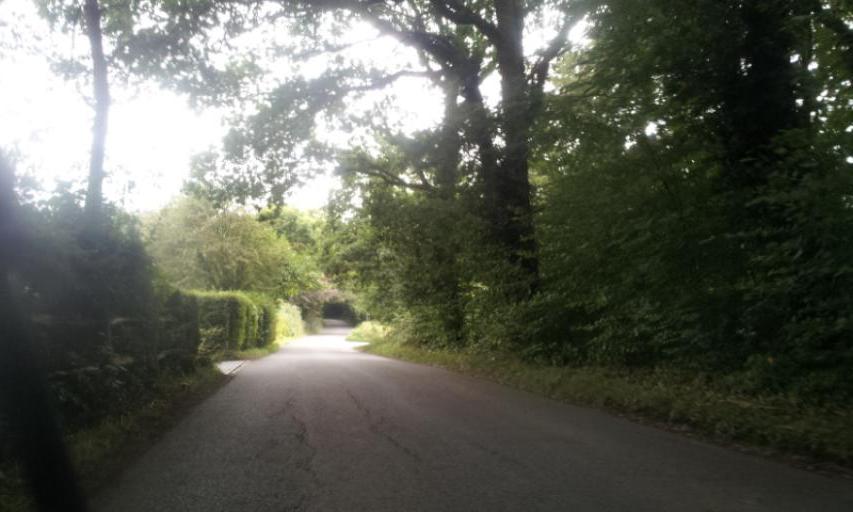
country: GB
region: England
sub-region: Kent
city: Hadlow
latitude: 51.2366
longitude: 0.3002
